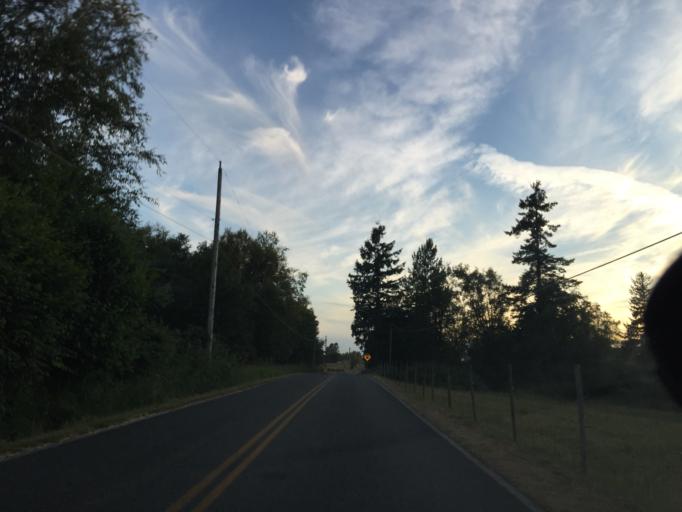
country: US
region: Washington
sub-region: Whatcom County
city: Everson
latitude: 48.9491
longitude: -122.3498
